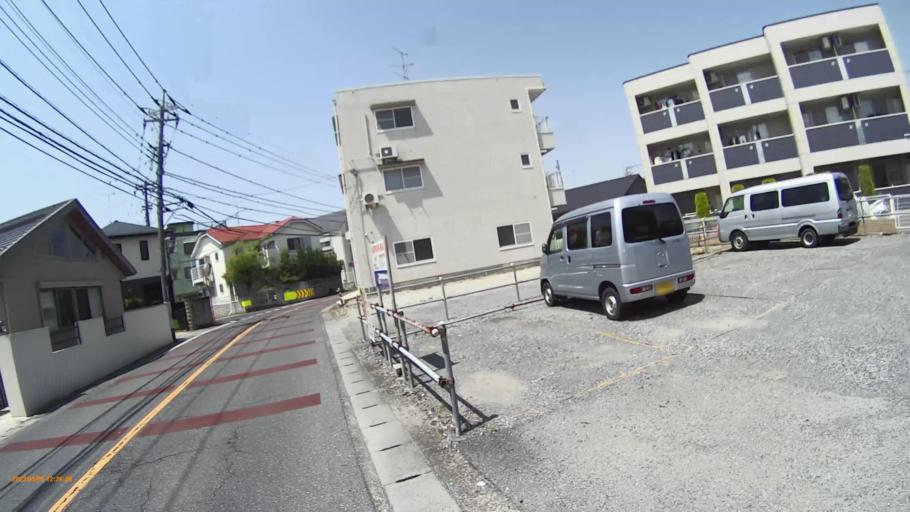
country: JP
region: Saitama
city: Koshigaya
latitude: 35.9320
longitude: 139.7783
